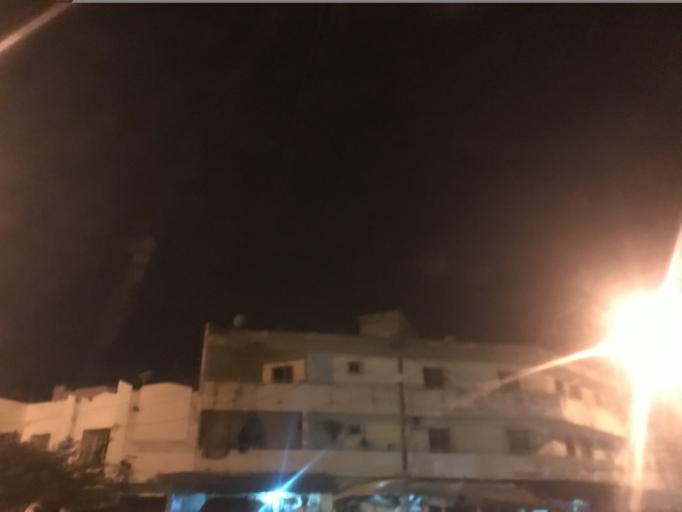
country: SN
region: Dakar
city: Grand Dakar
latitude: 14.7520
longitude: -17.4464
